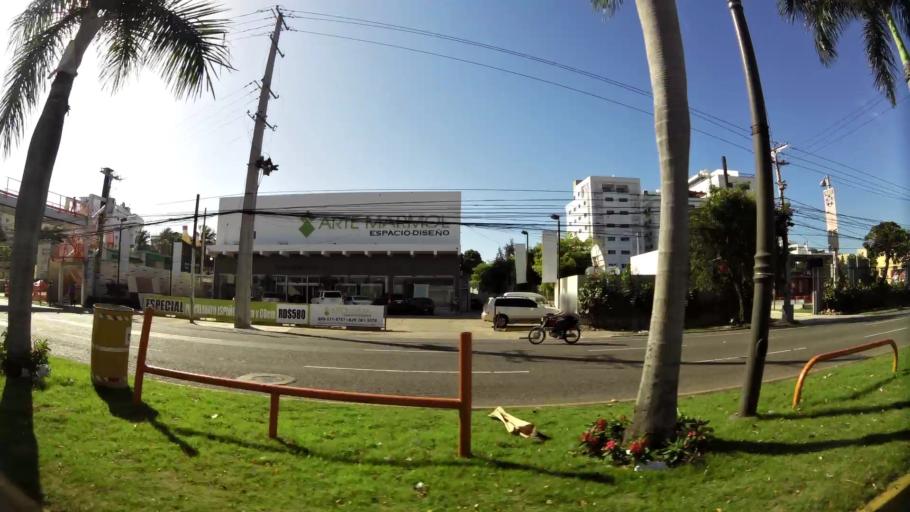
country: DO
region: Nacional
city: Bella Vista
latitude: 18.4502
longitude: -69.9664
